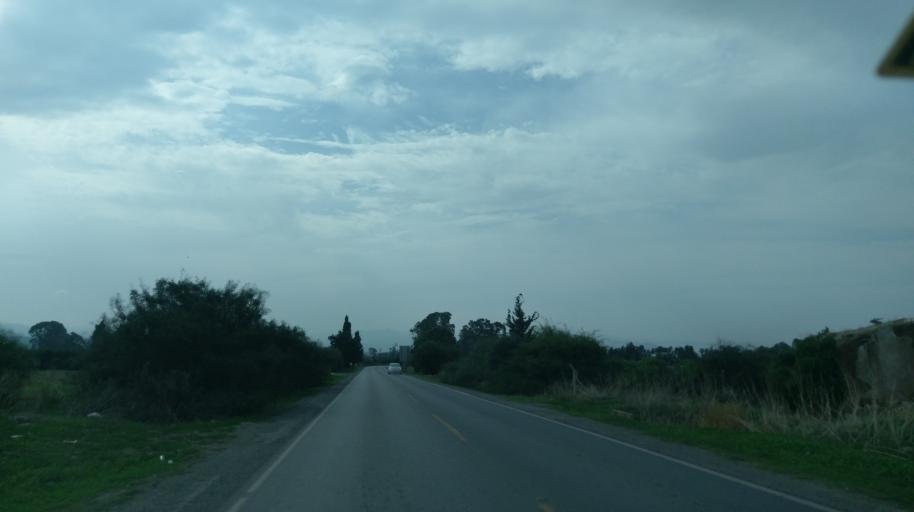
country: CY
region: Lefkosia
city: Lefka
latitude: 35.1604
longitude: 32.9003
